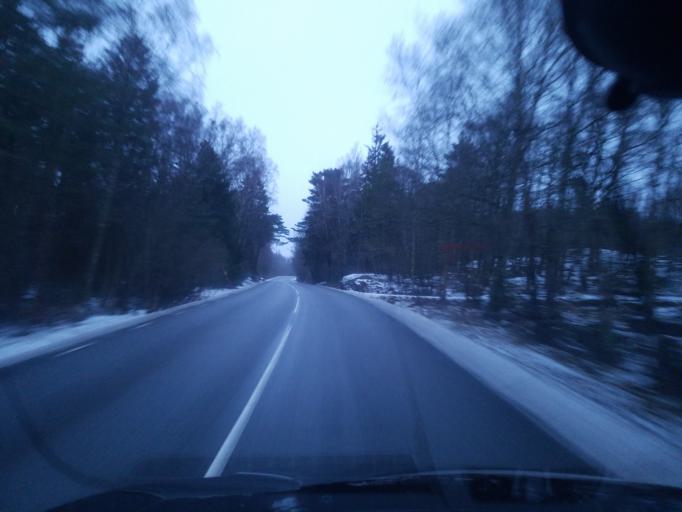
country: SE
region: Vaestra Goetaland
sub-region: Lysekils Kommun
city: Lysekil
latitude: 58.2988
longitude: 11.4767
